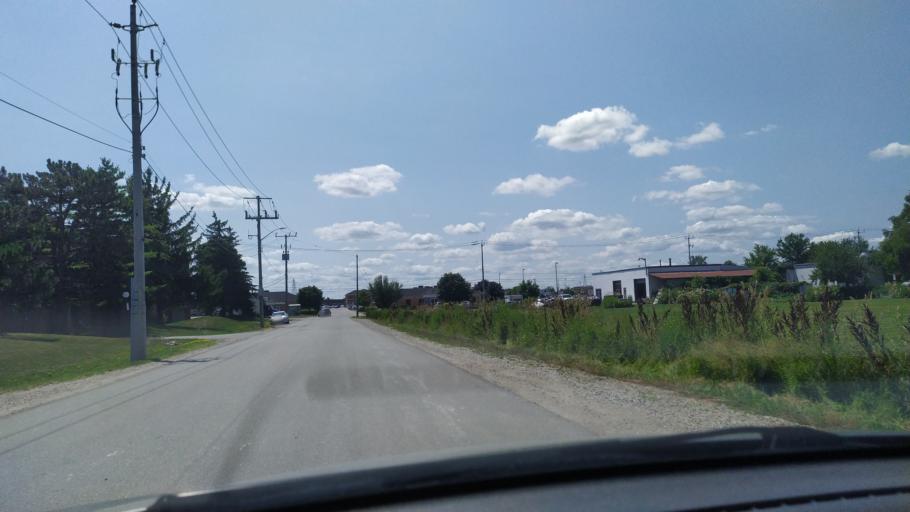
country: CA
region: Ontario
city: Stratford
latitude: 43.3558
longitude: -80.9930
